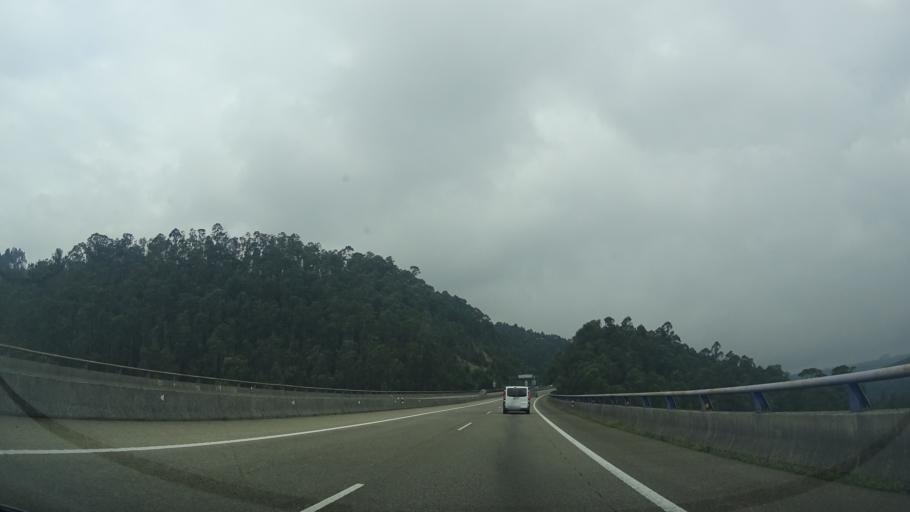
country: ES
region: Asturias
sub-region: Province of Asturias
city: Arriba
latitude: 43.4998
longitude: -5.5389
